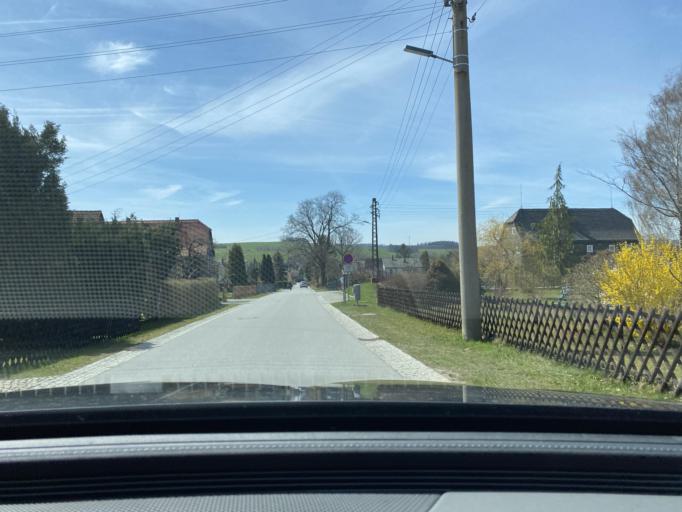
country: DE
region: Saxony
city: Eibau
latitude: 50.9994
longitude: 14.6452
